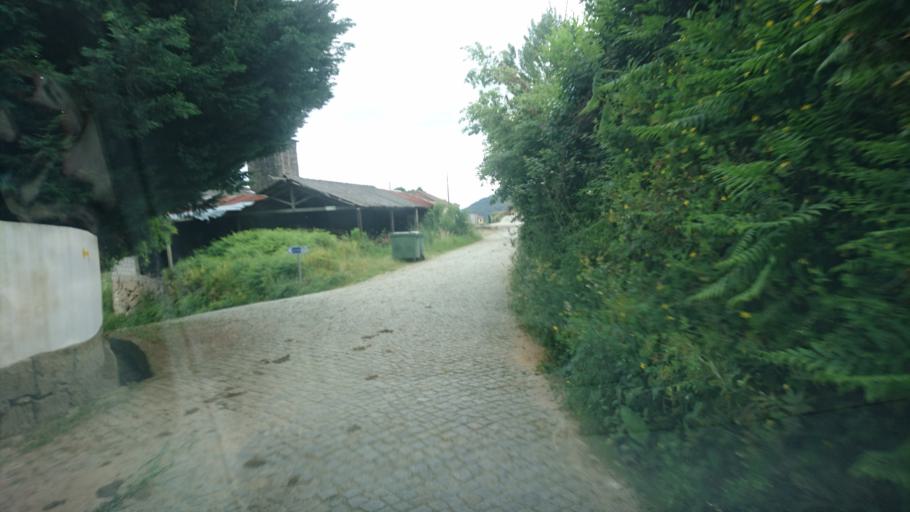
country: PT
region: Vila Real
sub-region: Mondim de Basto
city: Mondim de Basto
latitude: 41.4553
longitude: -7.9290
